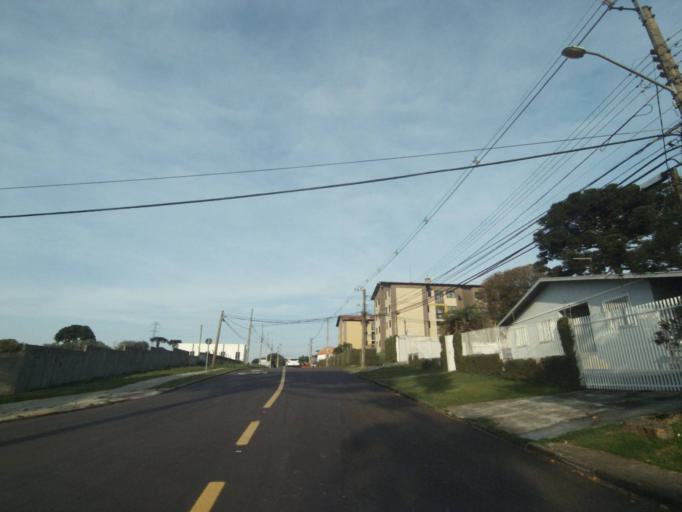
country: BR
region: Parana
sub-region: Curitiba
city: Curitiba
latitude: -25.4652
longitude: -49.3163
